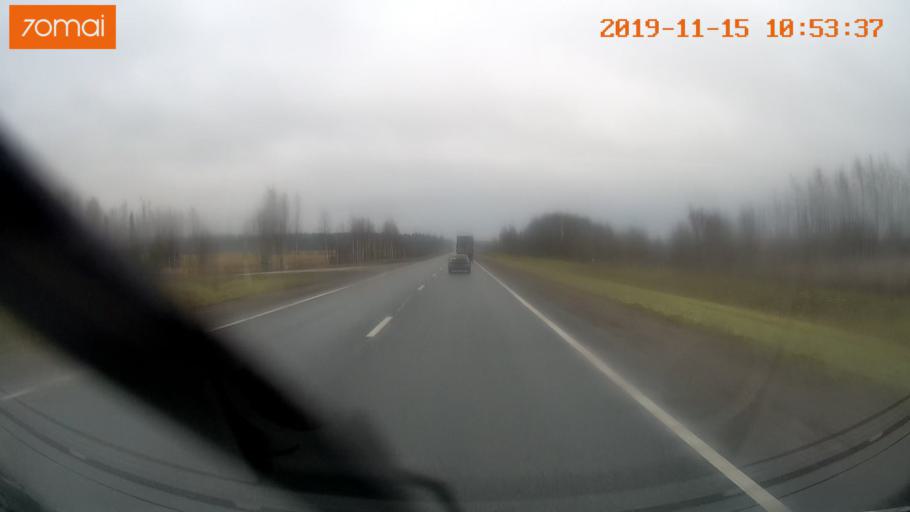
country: RU
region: Vologda
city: Chebsara
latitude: 59.1684
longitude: 38.7587
